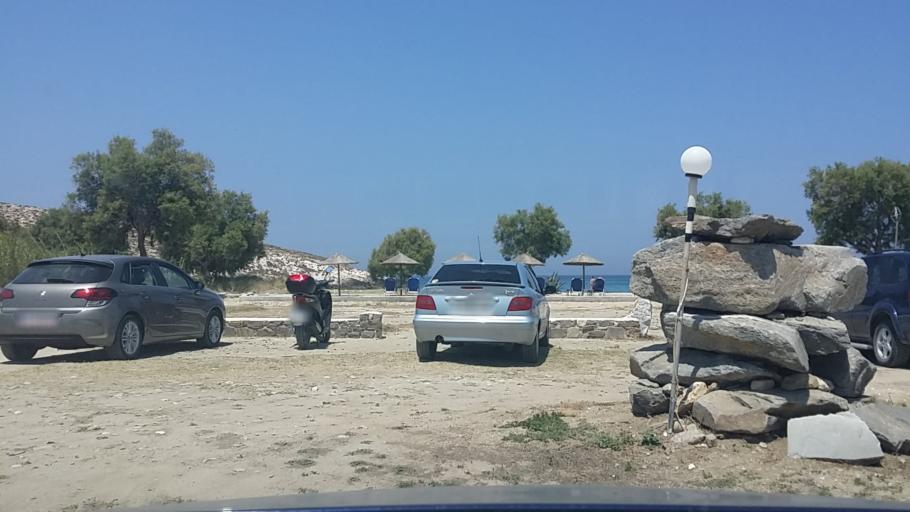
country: GR
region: South Aegean
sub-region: Nomos Kykladon
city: Paros
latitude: 37.0708
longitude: 25.1278
